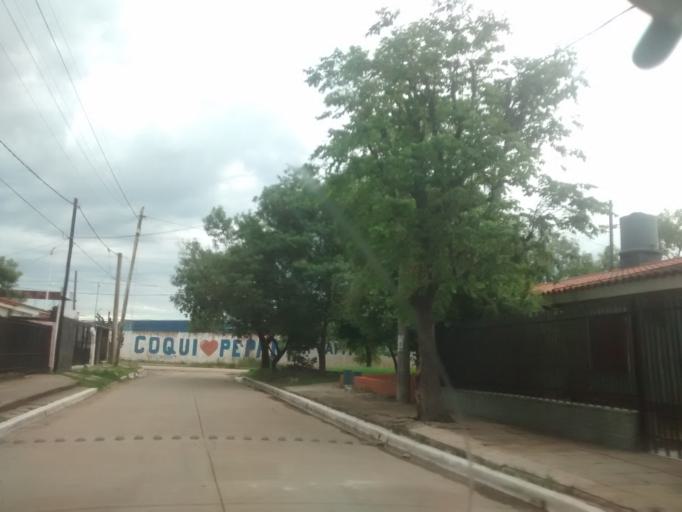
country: AR
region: Chaco
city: Fontana
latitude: -27.4406
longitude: -59.0150
